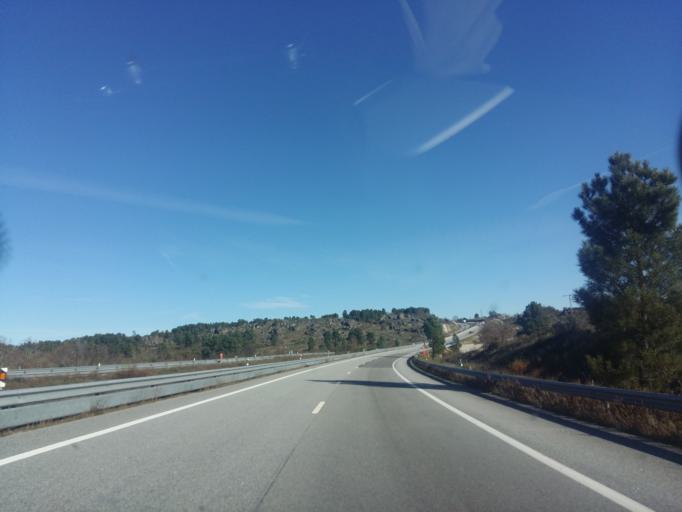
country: PT
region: Guarda
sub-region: Guarda
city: Sequeira
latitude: 40.5759
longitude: -7.1911
